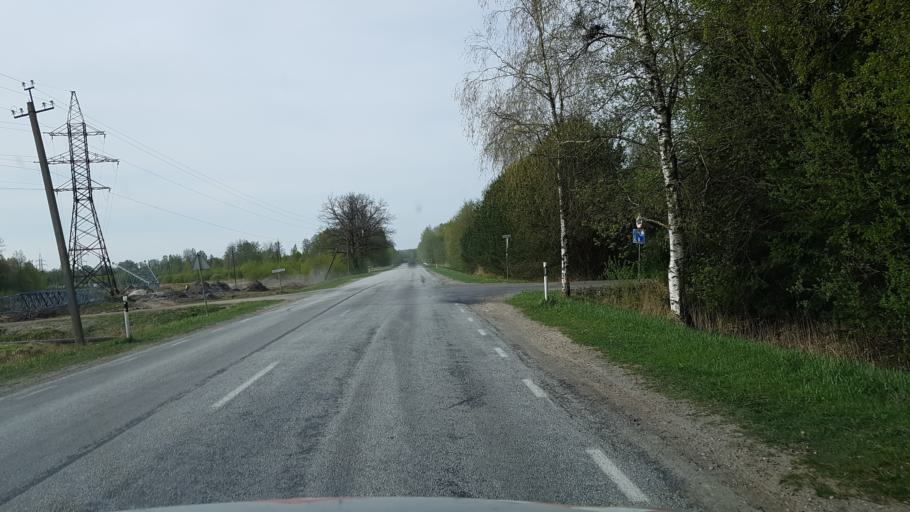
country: EE
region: Paernumaa
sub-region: Audru vald
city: Audru
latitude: 58.4127
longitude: 24.3097
